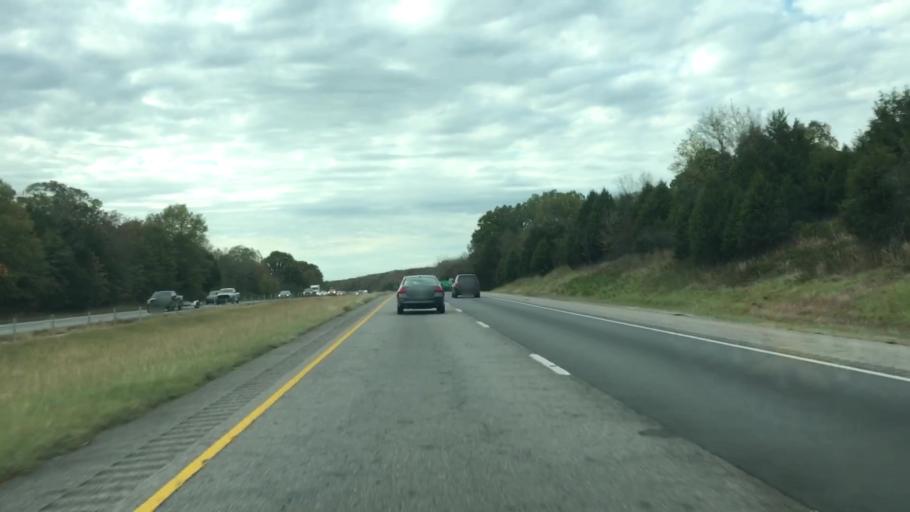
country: US
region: Arkansas
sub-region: Faulkner County
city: Conway
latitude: 35.1559
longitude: -92.5625
